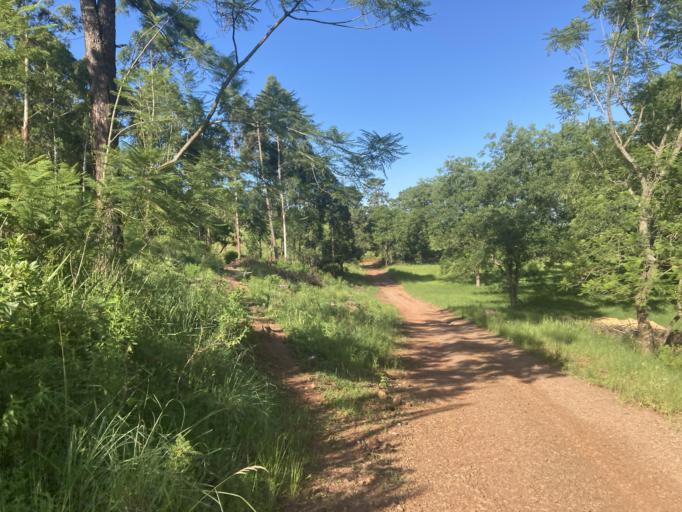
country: SZ
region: Hhohho
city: Lobamba
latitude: -26.4901
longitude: 31.1890
